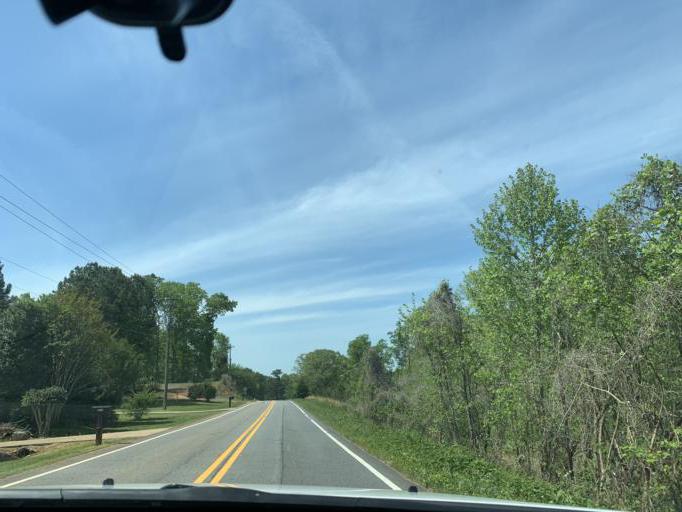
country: US
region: Georgia
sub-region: Forsyth County
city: Cumming
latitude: 34.2747
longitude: -84.2111
